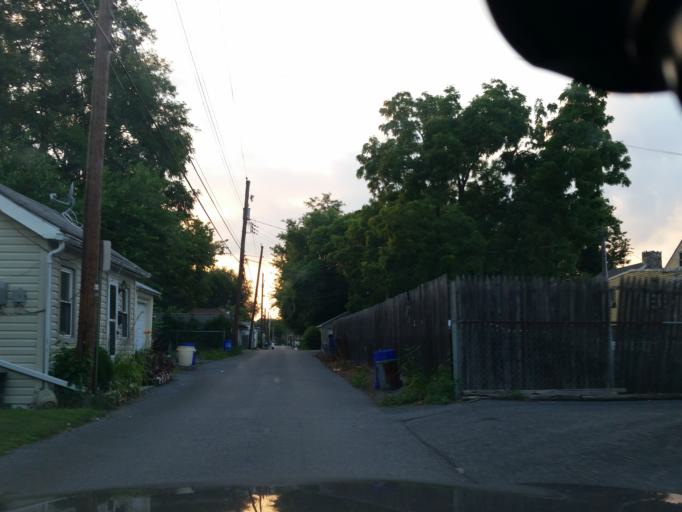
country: US
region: Pennsylvania
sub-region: Cumberland County
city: Lemoyne
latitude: 40.2554
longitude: -76.9002
